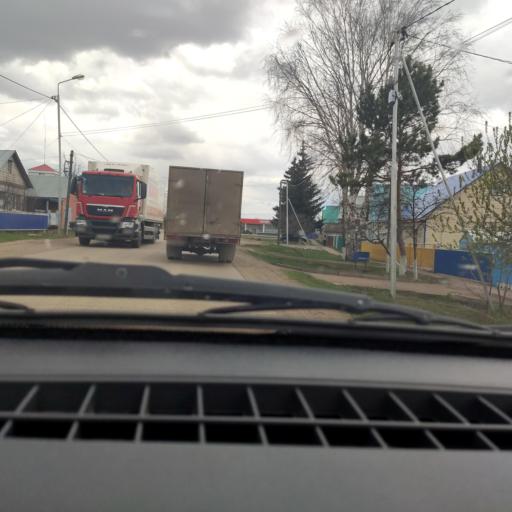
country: RU
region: Bashkortostan
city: Chekmagush
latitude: 55.1331
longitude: 54.6570
